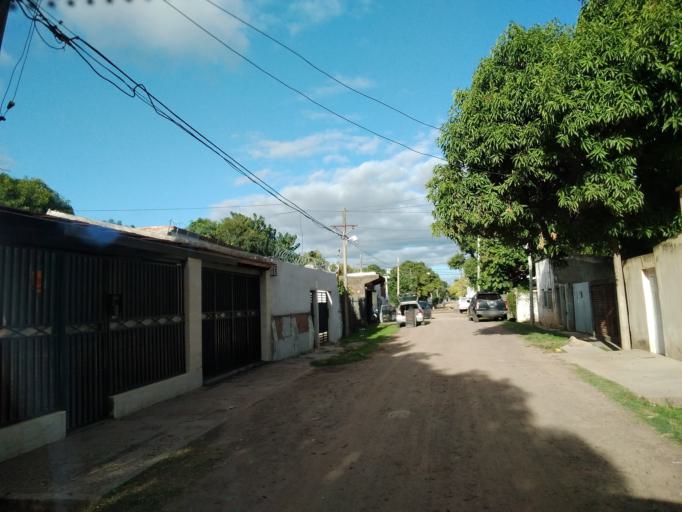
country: AR
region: Corrientes
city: Corrientes
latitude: -27.4779
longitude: -58.8118
